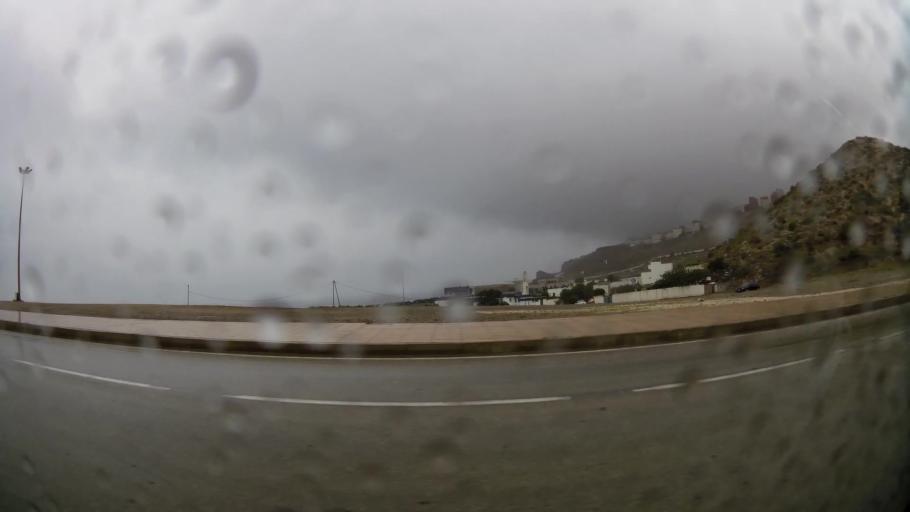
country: MA
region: Taza-Al Hoceima-Taounate
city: Al Hoceima
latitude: 35.2533
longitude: -3.9451
